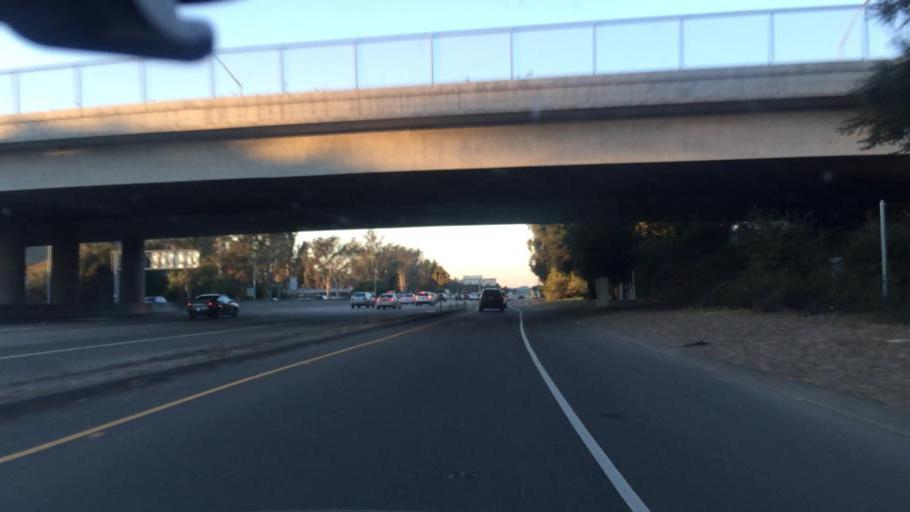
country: US
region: California
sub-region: Contra Costa County
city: San Ramon
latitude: 37.7796
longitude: -121.9761
